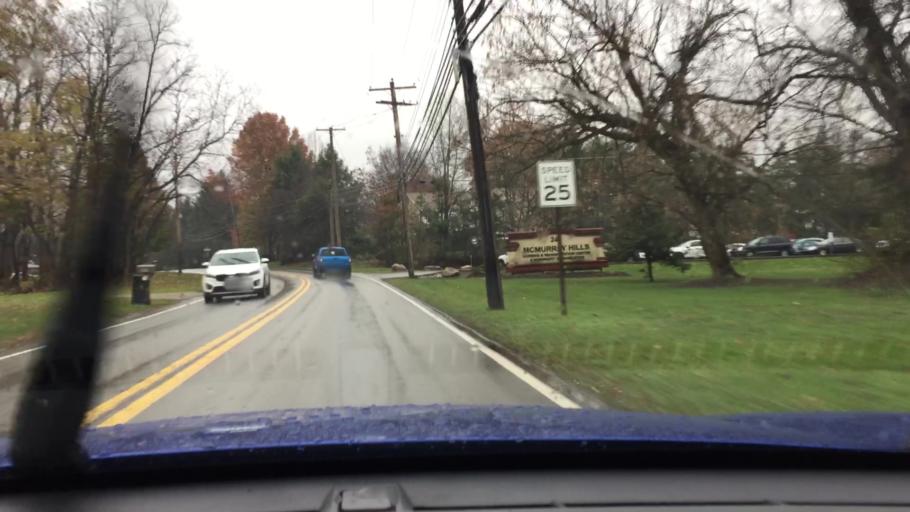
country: US
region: Pennsylvania
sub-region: Washington County
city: Thompsonville
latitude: 40.2755
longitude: -80.1339
